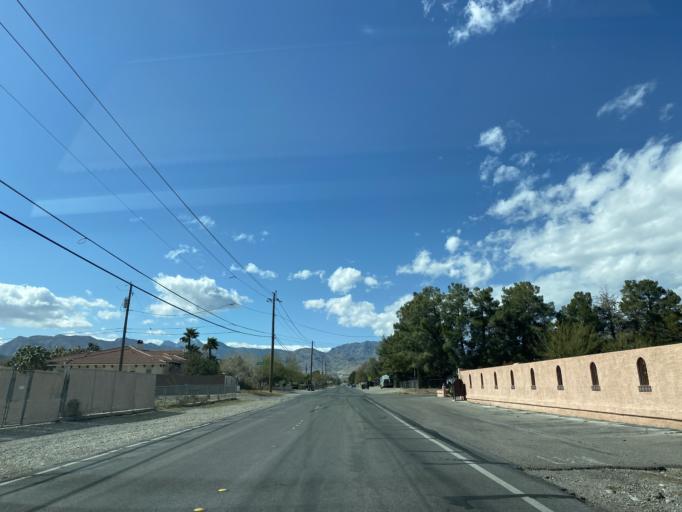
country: US
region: Nevada
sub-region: Clark County
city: Summerlin South
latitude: 36.2557
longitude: -115.2852
